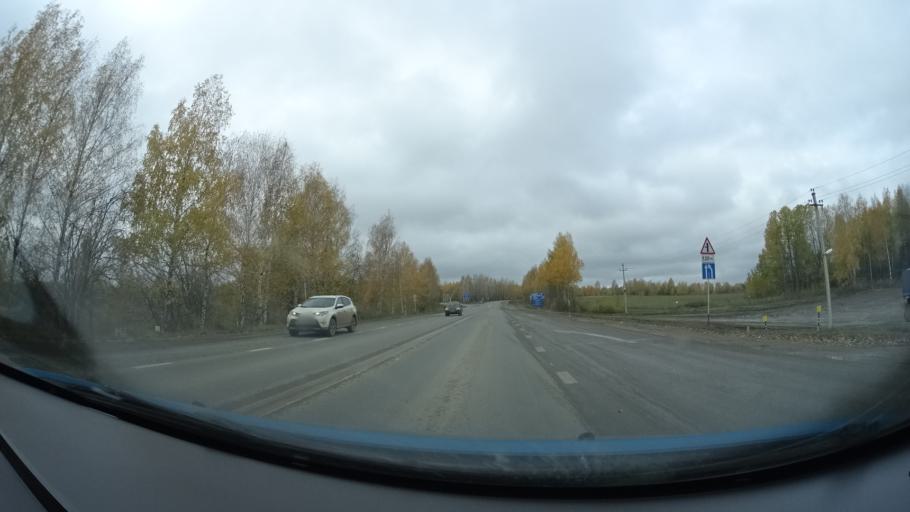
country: RU
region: Perm
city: Osa
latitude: 57.1793
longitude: 55.5379
